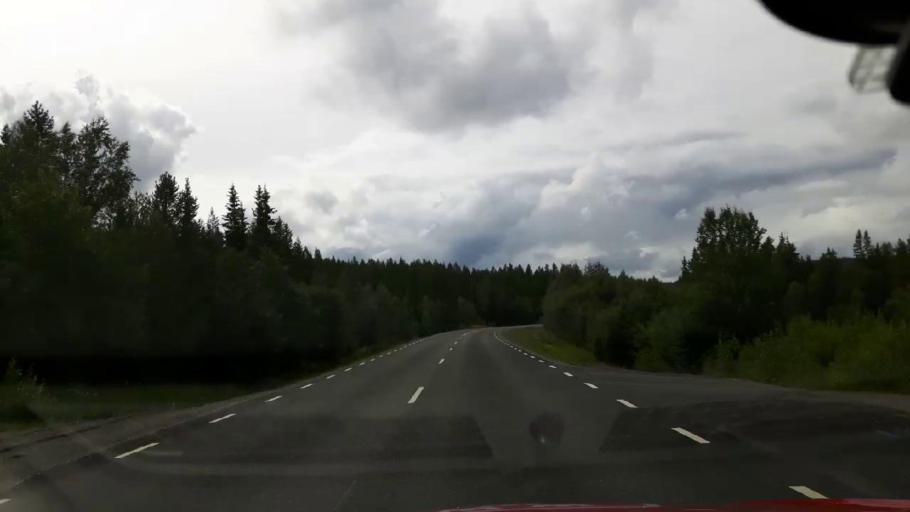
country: NO
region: Nord-Trondelag
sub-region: Lierne
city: Sandvika
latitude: 64.6308
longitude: 14.1359
